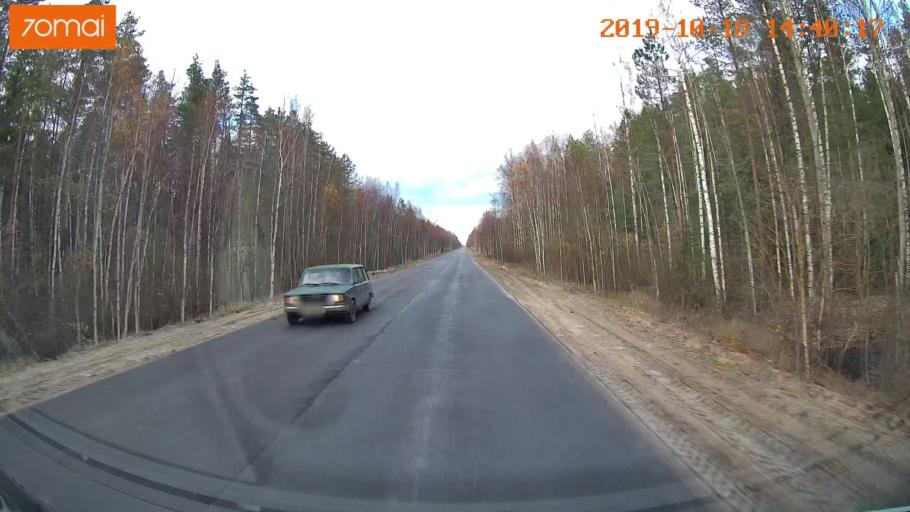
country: RU
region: Vladimir
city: Velikodvorskiy
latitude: 55.2742
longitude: 40.6687
